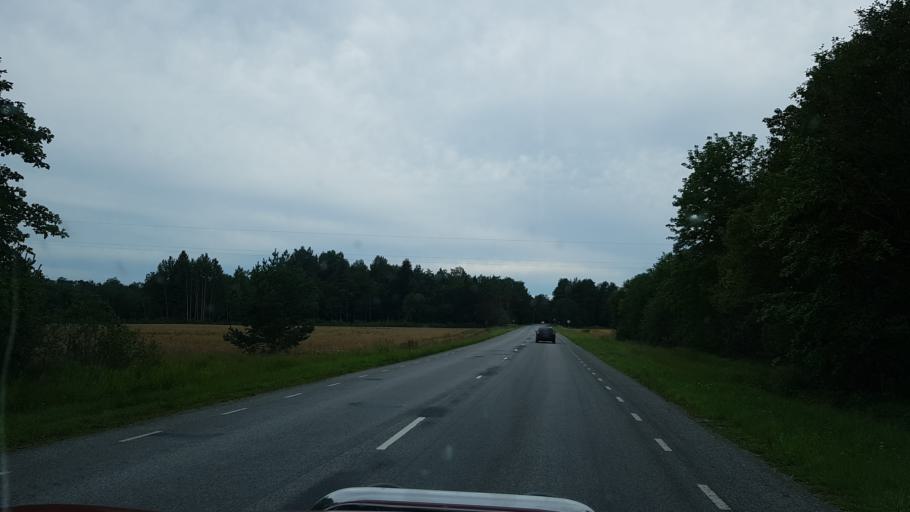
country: EE
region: Laeaene
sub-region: Ridala Parish
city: Uuemoisa
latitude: 58.9978
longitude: 23.7266
